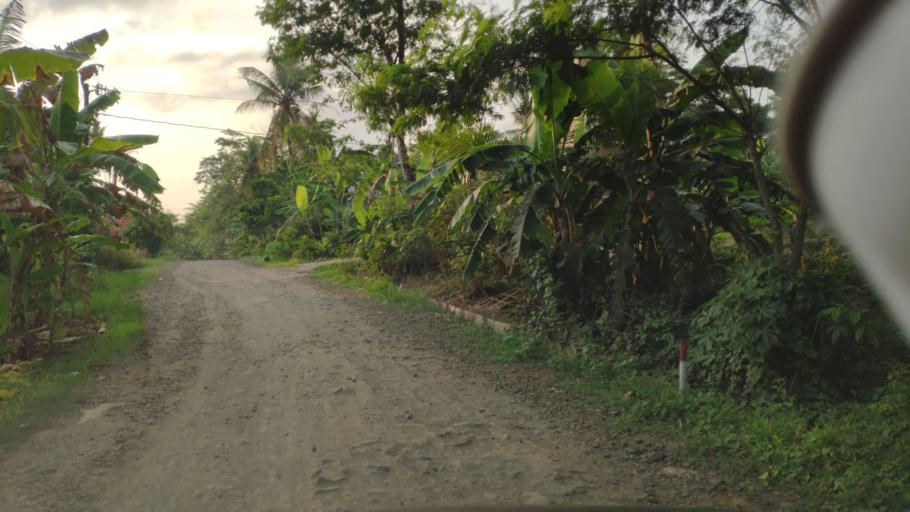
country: ID
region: Central Java
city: Jeruklegi
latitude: -7.6613
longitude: 108.9782
